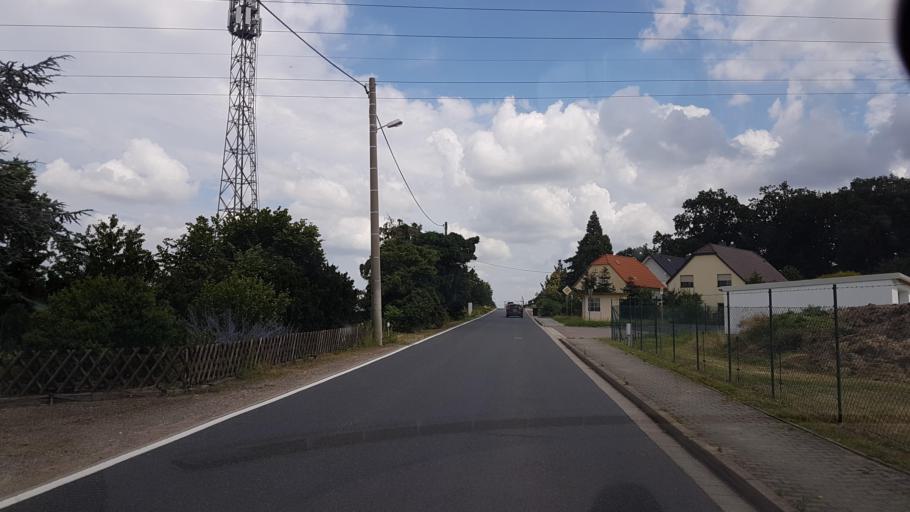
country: DE
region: Saxony
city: Weissig
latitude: 51.2686
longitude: 13.4647
